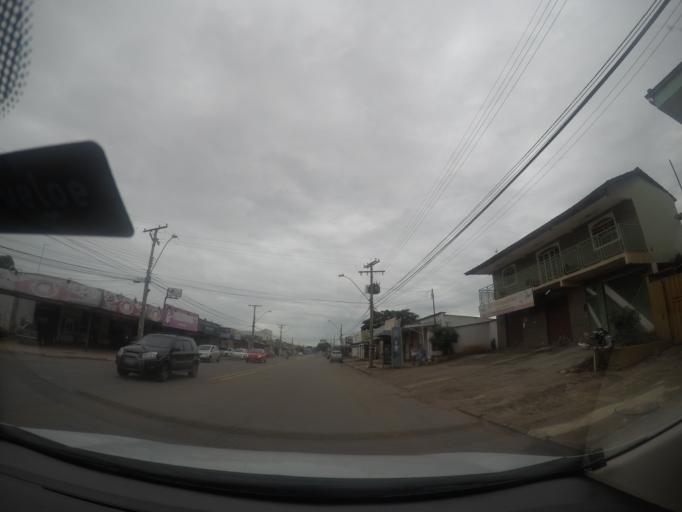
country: BR
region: Goias
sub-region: Goiania
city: Goiania
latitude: -16.6177
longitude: -49.2921
